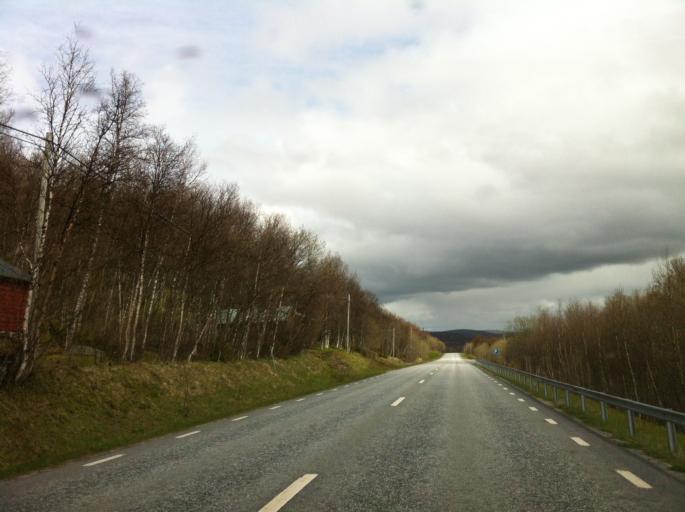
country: NO
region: Sor-Trondelag
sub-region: Tydal
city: Aas
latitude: 62.5550
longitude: 12.2790
